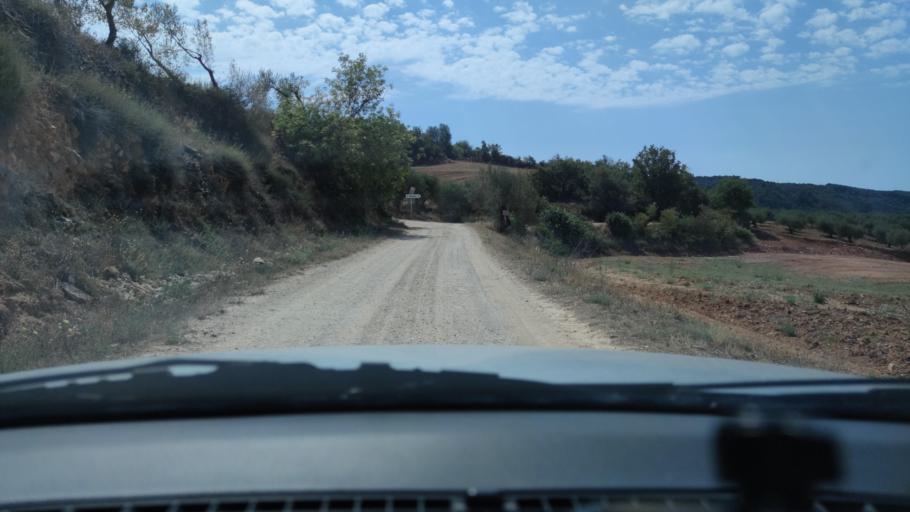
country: ES
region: Catalonia
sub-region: Provincia de Lleida
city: Ager
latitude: 41.9320
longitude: 0.8059
